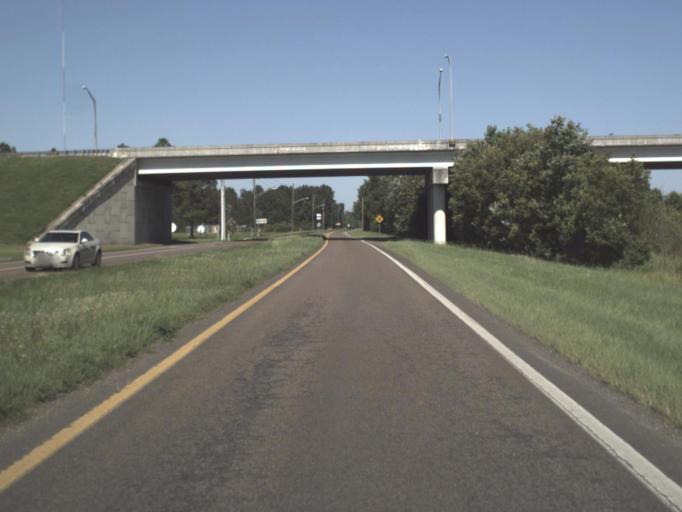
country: US
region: Florida
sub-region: Duval County
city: Baldwin
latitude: 30.3041
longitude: -81.9431
